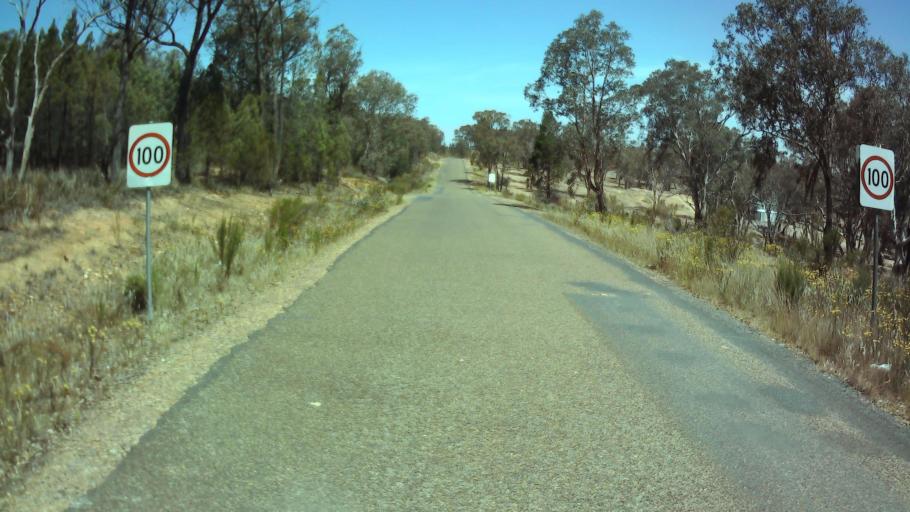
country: AU
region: New South Wales
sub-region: Weddin
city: Grenfell
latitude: -33.9043
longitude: 148.1783
